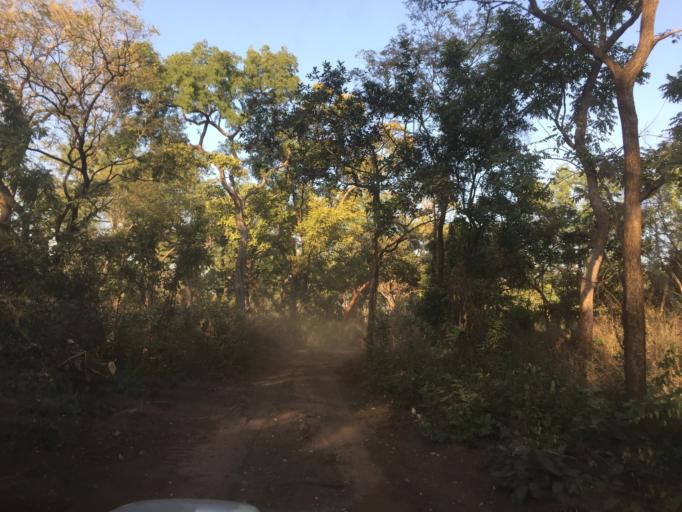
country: GW
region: Oio
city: Farim
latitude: 12.5271
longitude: -15.2799
